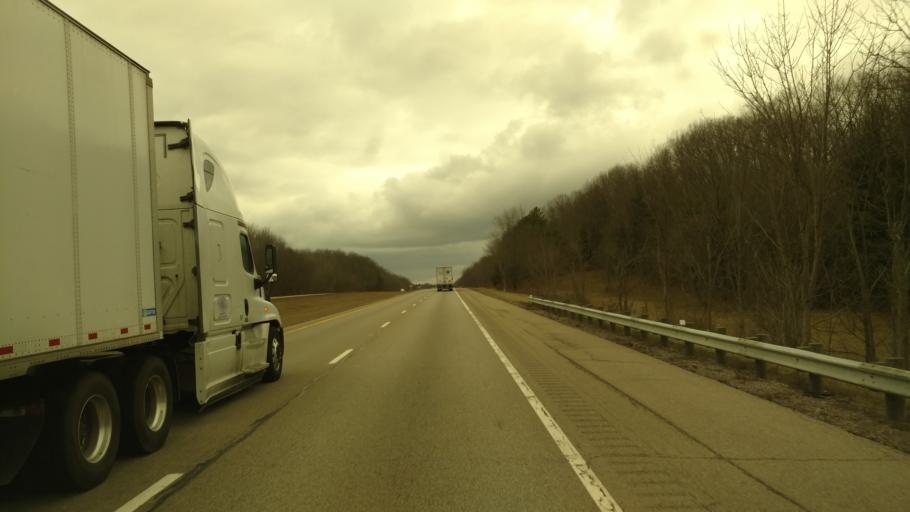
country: US
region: Ohio
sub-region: Muskingum County
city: Zanesville
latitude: 39.9458
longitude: -82.1163
